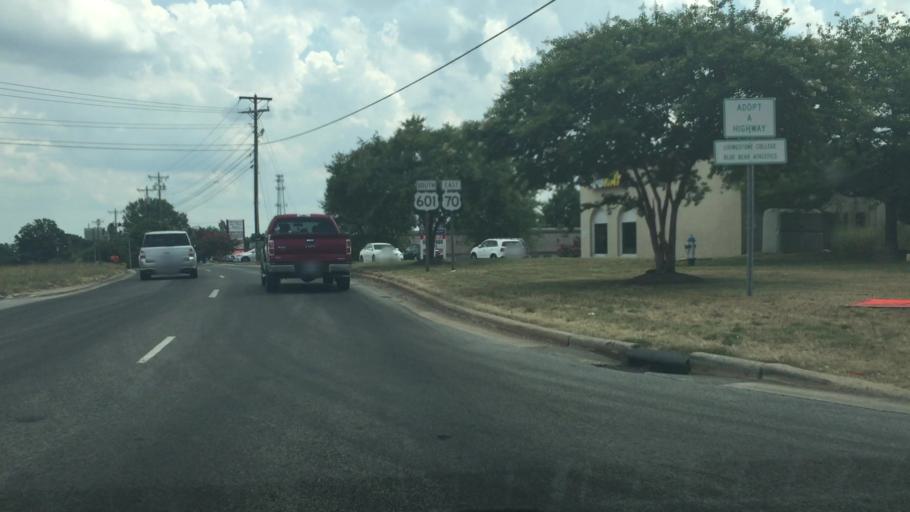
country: US
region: North Carolina
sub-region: Rowan County
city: Franklin
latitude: 35.6937
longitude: -80.5129
